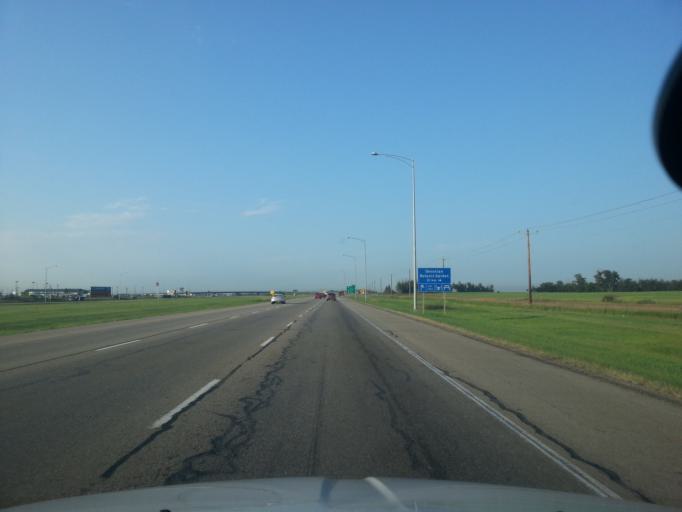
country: CA
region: Alberta
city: Leduc
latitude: 53.3483
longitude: -113.5445
